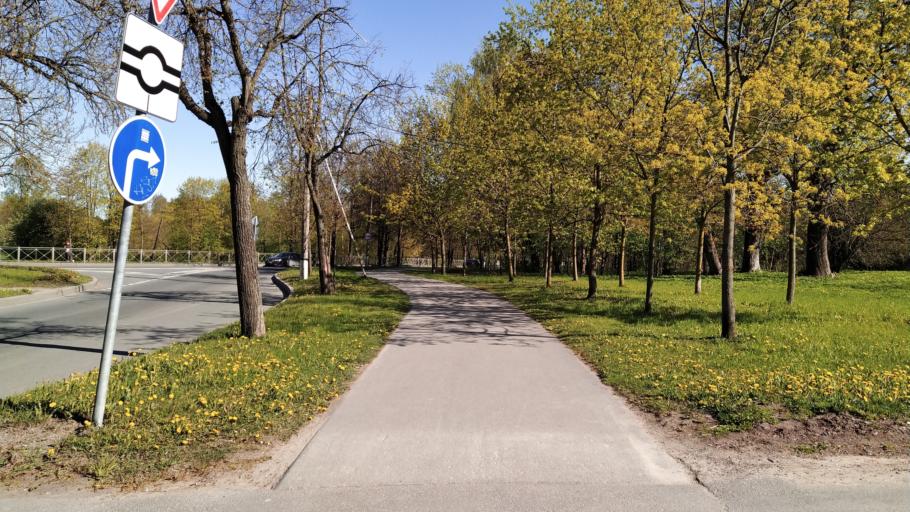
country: RU
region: St.-Petersburg
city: Pavlovsk
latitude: 59.7022
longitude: 30.4201
